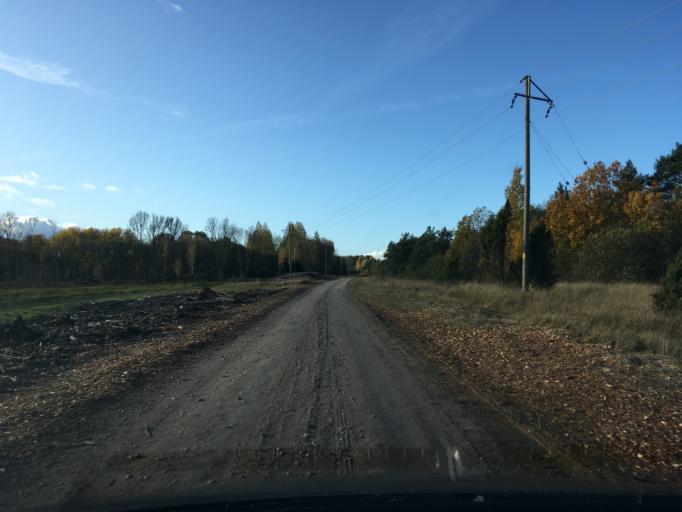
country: EE
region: Laeaene
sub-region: Lihula vald
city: Lihula
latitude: 58.5649
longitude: 23.7703
